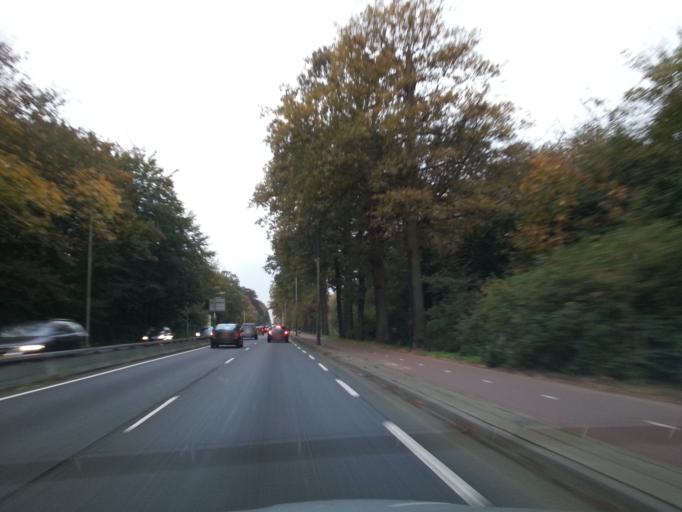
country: NL
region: South Holland
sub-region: Gemeente Wassenaar
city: Wassenaar
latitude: 52.1357
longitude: 4.4030
